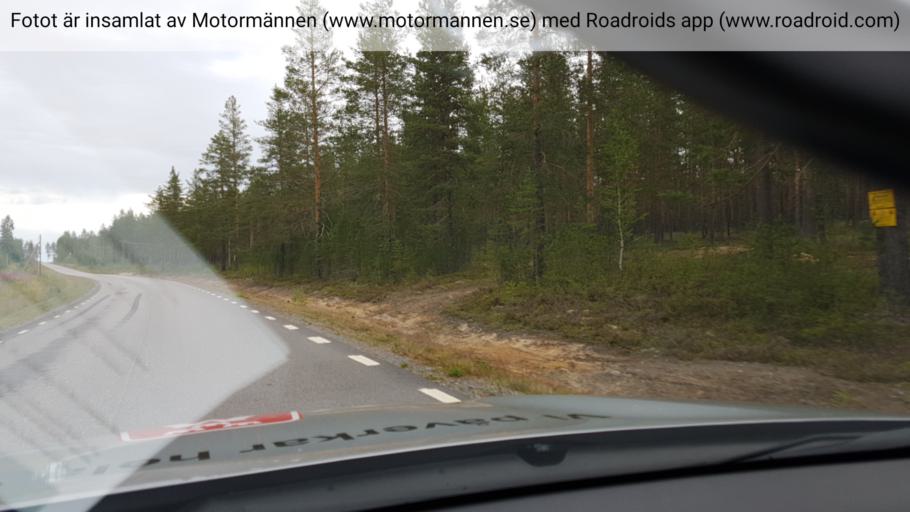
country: SE
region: Norrbotten
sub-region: Bodens Kommun
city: Boden
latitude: 65.7887
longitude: 21.6438
